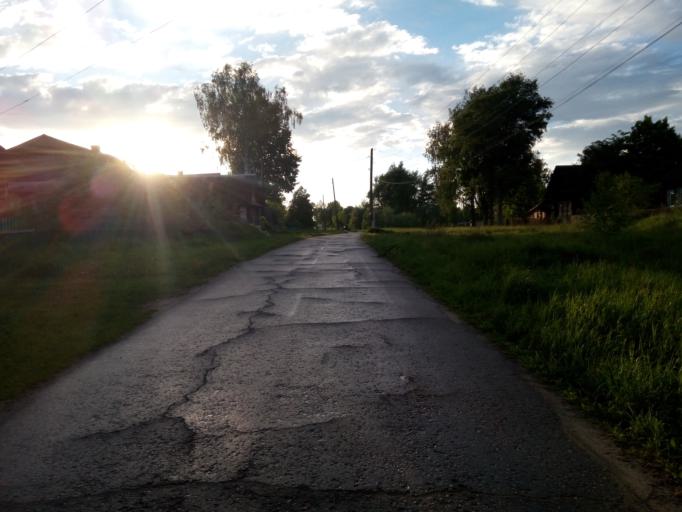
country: RU
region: Nizjnij Novgorod
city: Voskresenskoye
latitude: 56.7717
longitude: 45.5544
